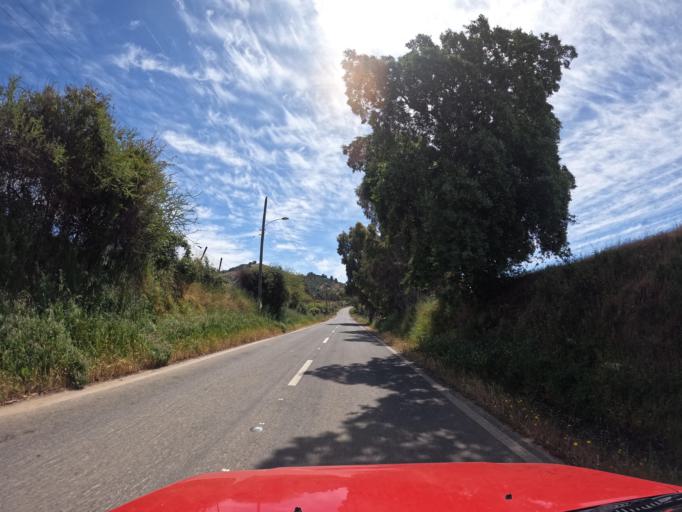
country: CL
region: Maule
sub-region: Provincia de Talca
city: Talca
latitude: -35.0544
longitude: -71.7463
